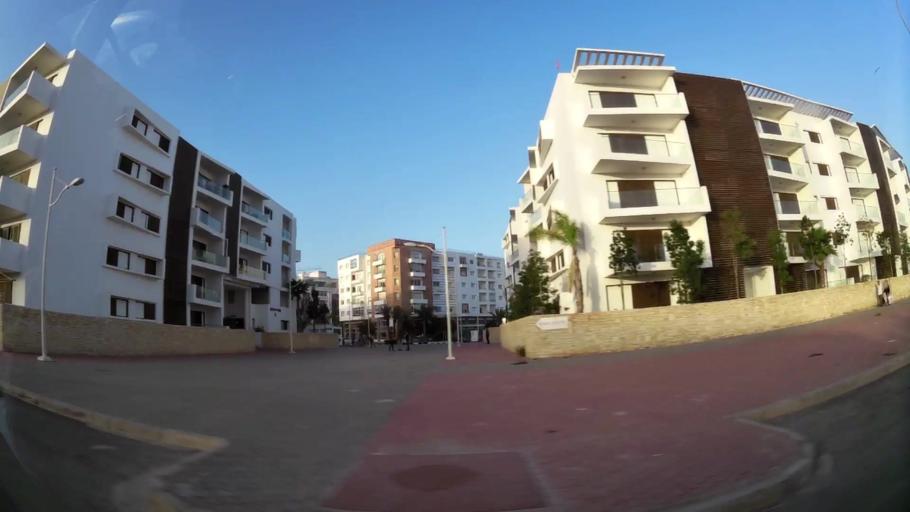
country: MA
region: Souss-Massa-Draa
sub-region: Agadir-Ida-ou-Tnan
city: Agadir
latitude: 30.3984
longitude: -9.5891
